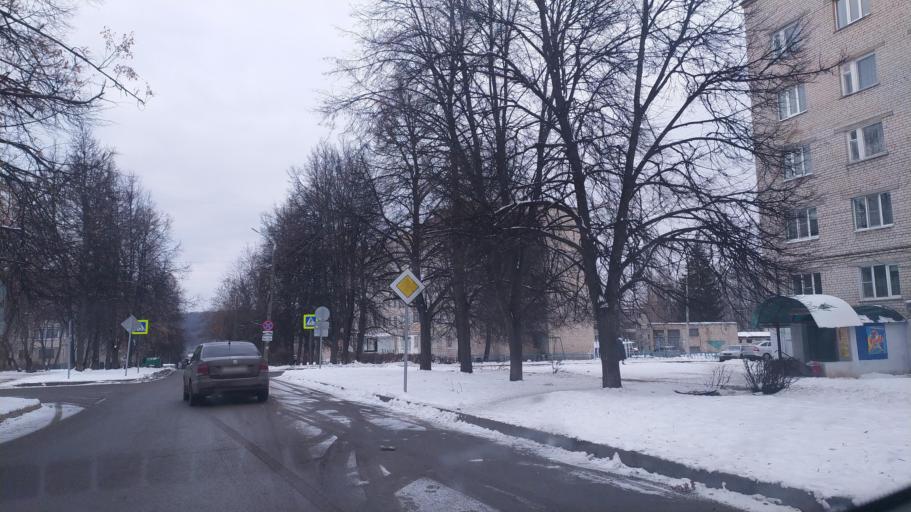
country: RU
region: Chuvashia
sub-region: Cheboksarskiy Rayon
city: Cheboksary
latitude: 56.1246
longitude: 47.1989
